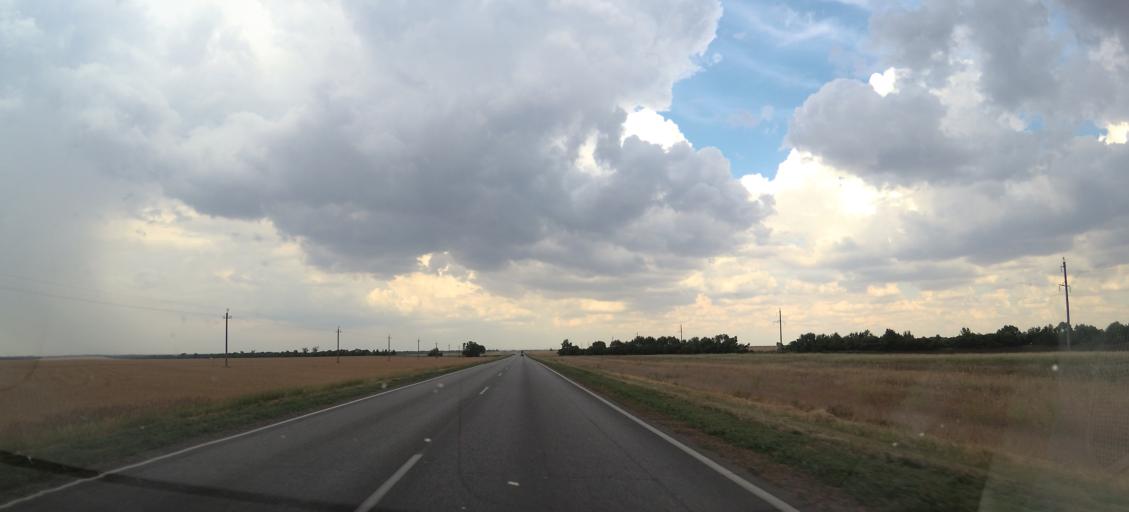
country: RU
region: Rostov
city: Orlovskiy
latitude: 46.9363
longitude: 42.1109
